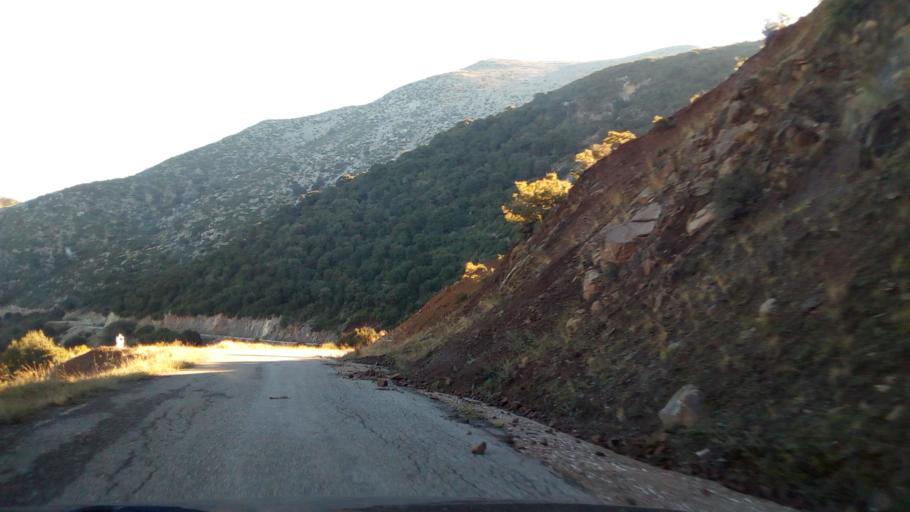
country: GR
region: West Greece
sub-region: Nomos Aitolias kai Akarnanias
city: Nafpaktos
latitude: 38.5086
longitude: 21.8395
